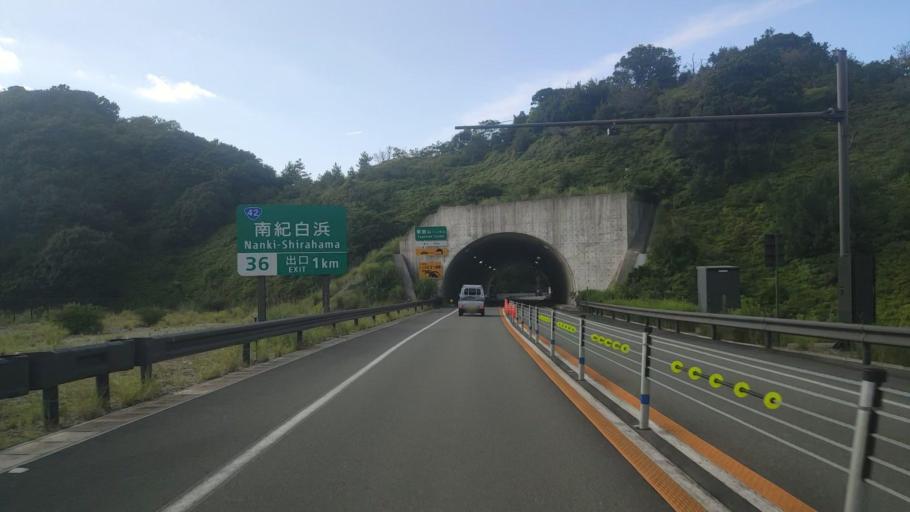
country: JP
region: Wakayama
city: Tanabe
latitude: 33.6380
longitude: 135.4098
